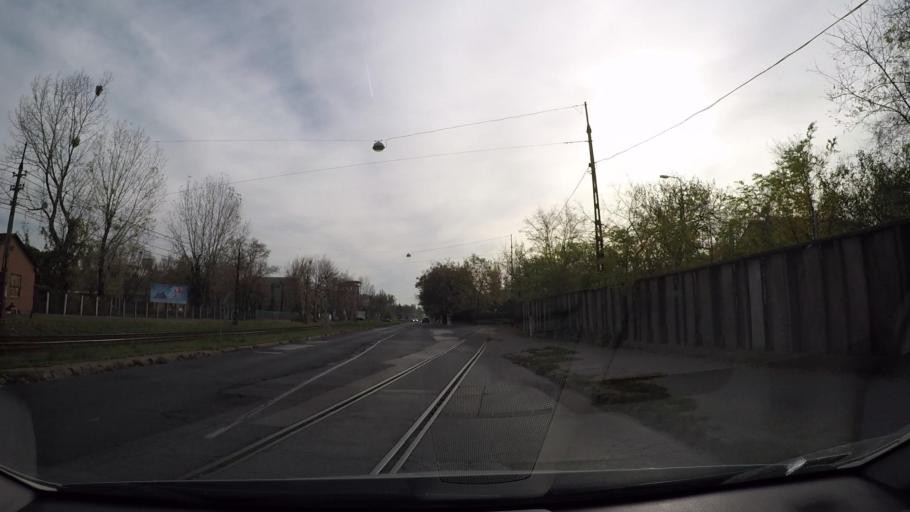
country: HU
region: Budapest
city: Budapest X. keruelet
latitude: 47.4891
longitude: 19.1499
